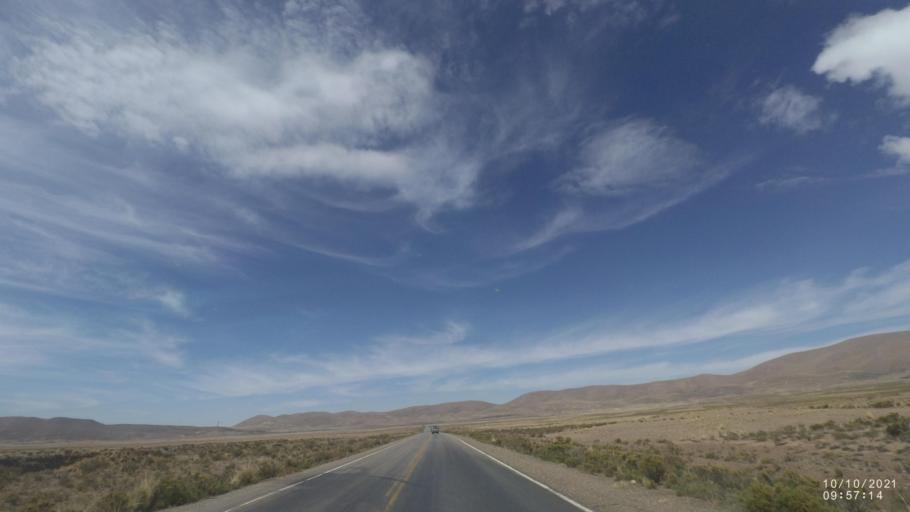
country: BO
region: La Paz
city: Colquiri
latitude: -17.3333
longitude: -67.3829
